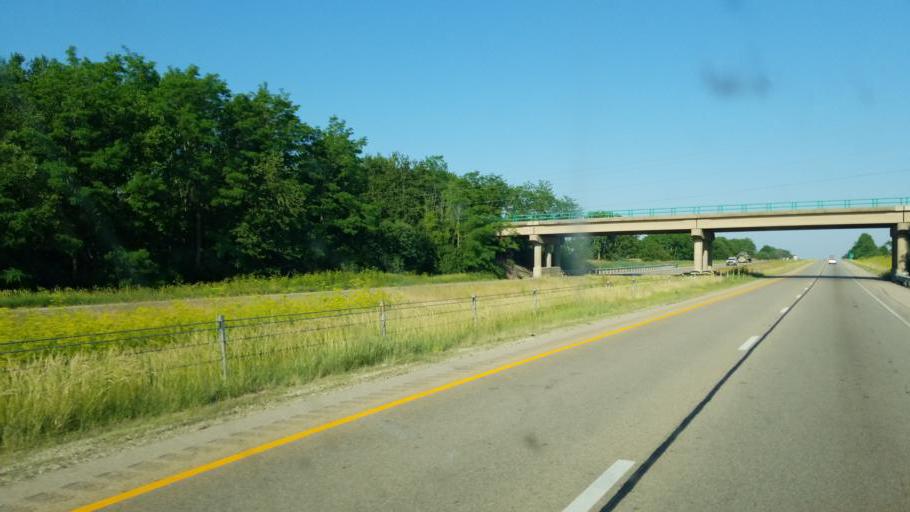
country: US
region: Illinois
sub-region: LaSalle County
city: Ottawa
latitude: 41.3765
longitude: -88.8159
